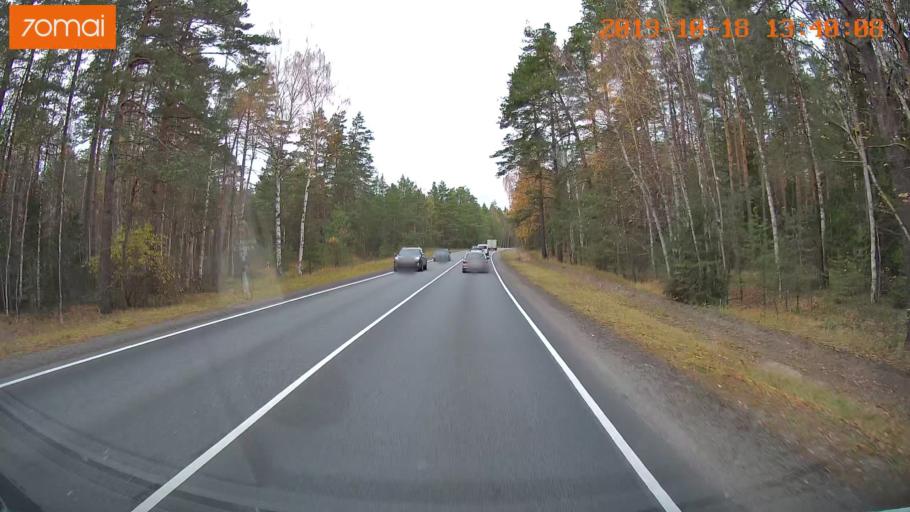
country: RU
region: Rjazan
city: Solotcha
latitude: 54.9061
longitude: 40.0001
